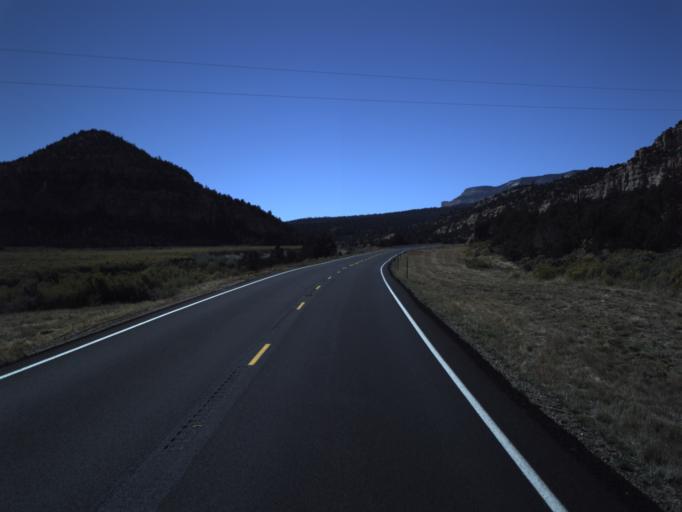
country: US
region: Utah
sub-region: Garfield County
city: Panguitch
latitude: 37.7304
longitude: -111.7600
